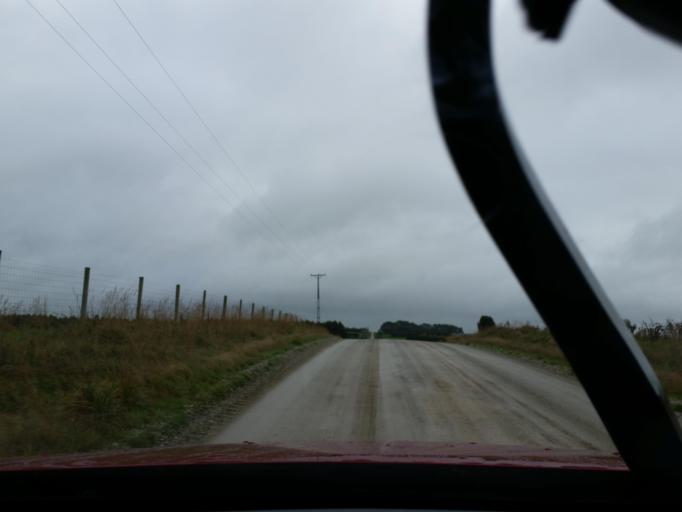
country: NZ
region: Southland
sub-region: Invercargill City
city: Invercargill
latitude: -46.2850
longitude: 168.4871
